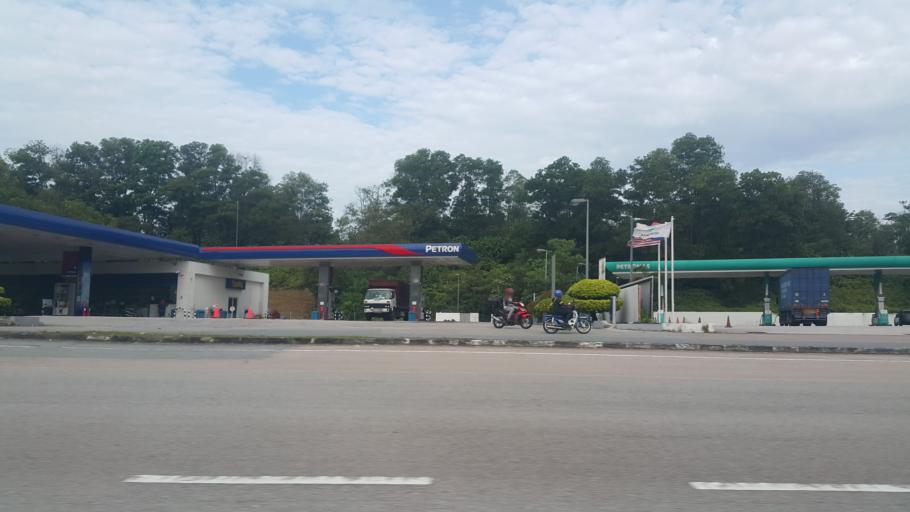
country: MY
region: Johor
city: Pekan Nenas
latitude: 1.4000
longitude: 103.5876
